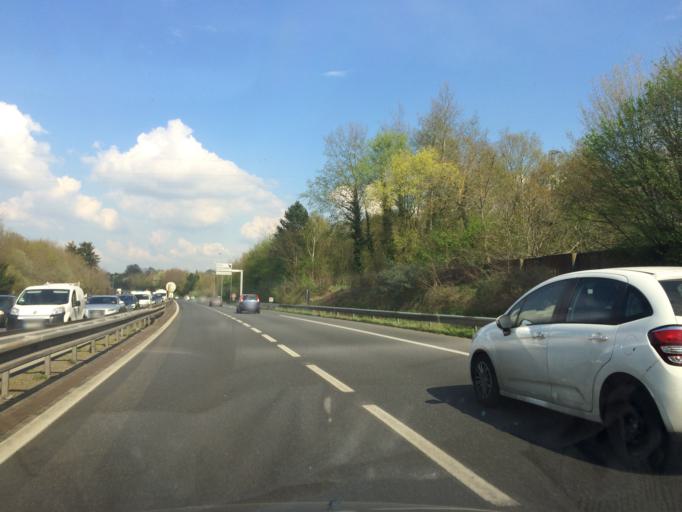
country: FR
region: Pays de la Loire
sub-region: Departement de la Loire-Atlantique
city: La Chapelle-sur-Erdre
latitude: 47.2761
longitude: -1.5223
